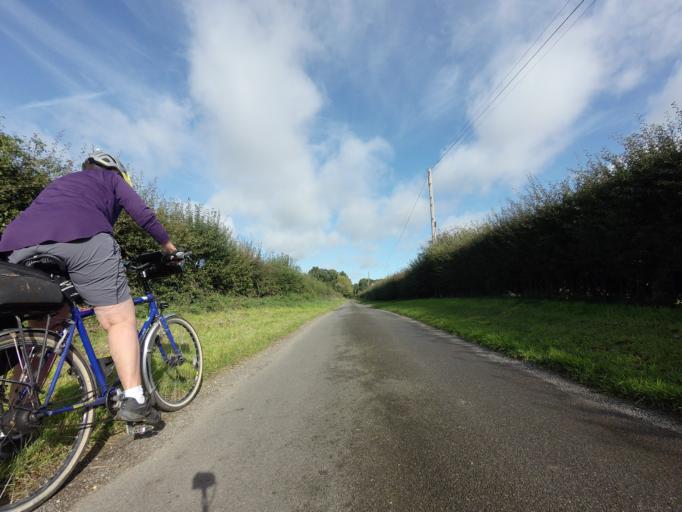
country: GB
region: England
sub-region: Norfolk
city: Fakenham
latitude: 52.8838
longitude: 0.6842
